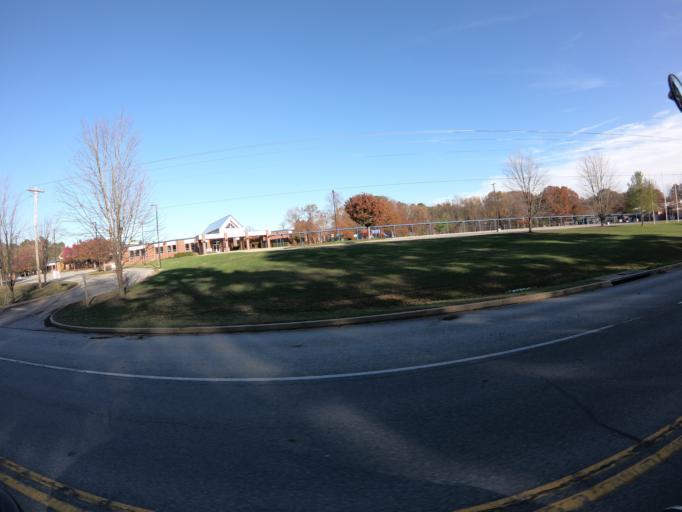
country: US
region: Maryland
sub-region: Saint Mary's County
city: Leonardtown
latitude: 38.3293
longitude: -76.6769
